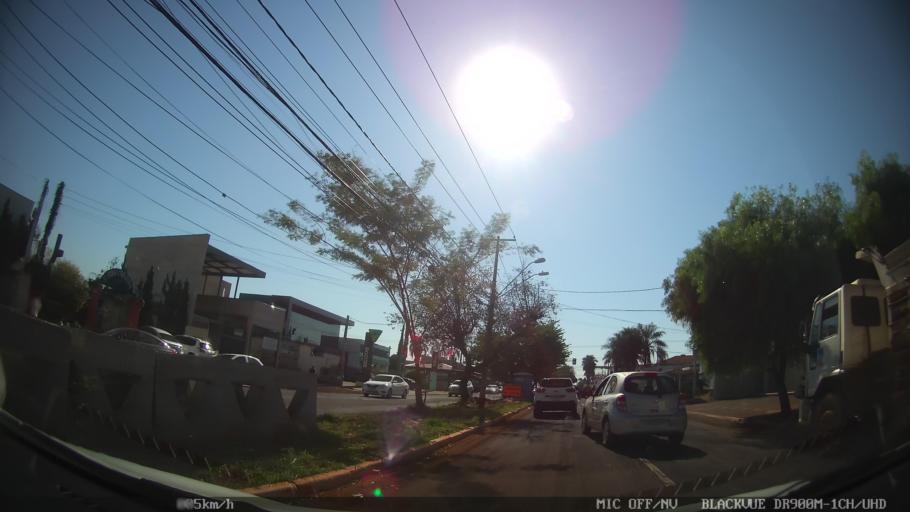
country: BR
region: Sao Paulo
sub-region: Ribeirao Preto
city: Ribeirao Preto
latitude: -21.1956
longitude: -47.8133
